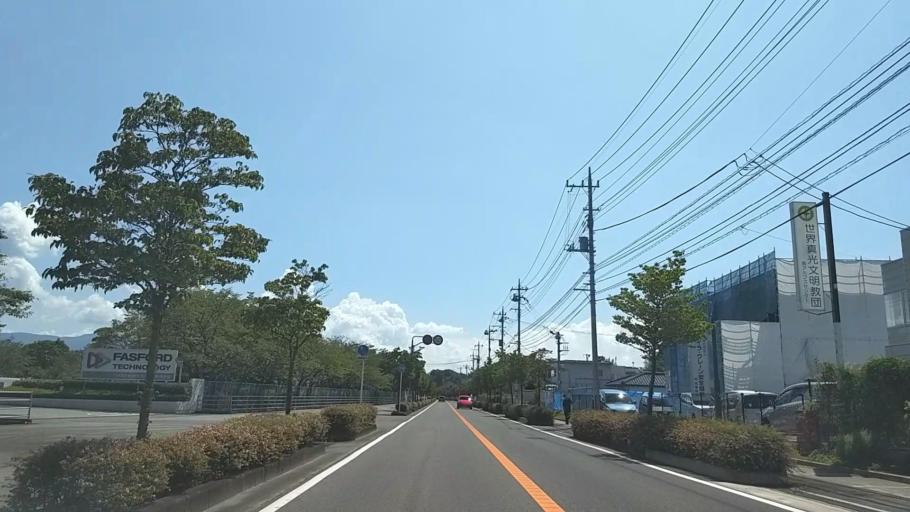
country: JP
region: Yamanashi
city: Ryuo
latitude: 35.6326
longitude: 138.4984
